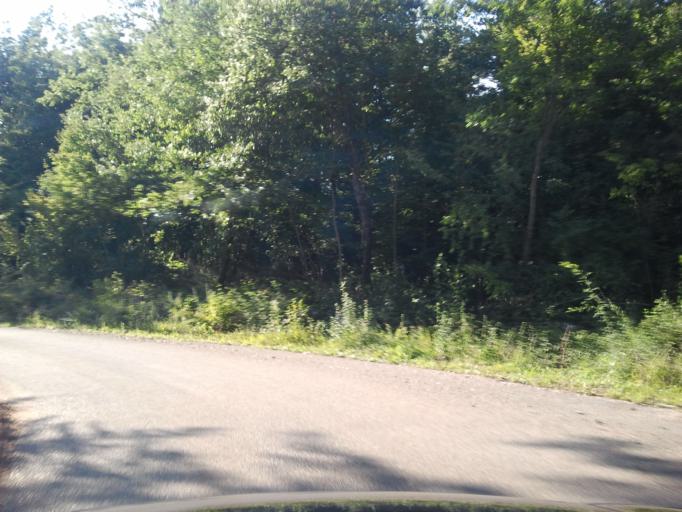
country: HR
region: Zadarska
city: Gracac
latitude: 44.3831
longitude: 15.7069
